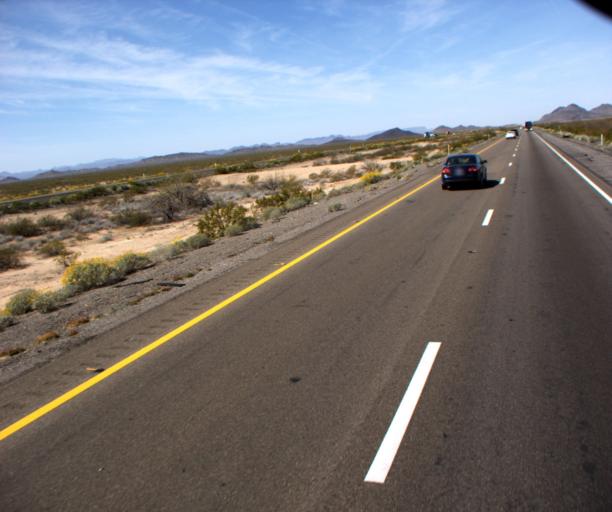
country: US
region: Arizona
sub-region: La Paz County
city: Salome
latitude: 33.5988
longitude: -113.5494
